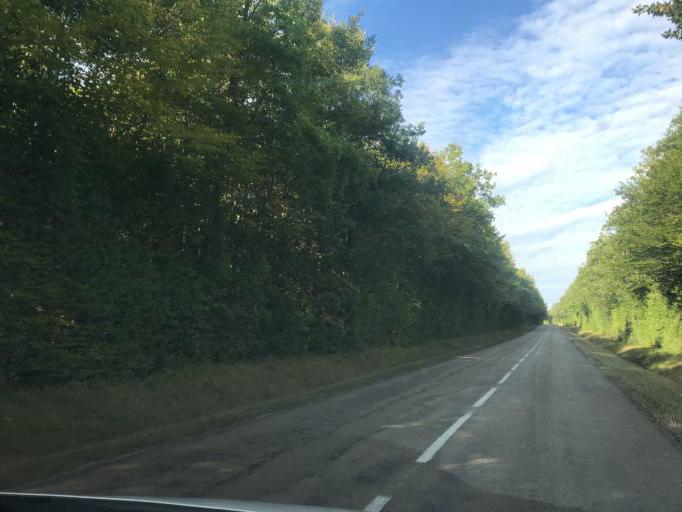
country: FR
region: Bourgogne
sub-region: Departement de l'Yonne
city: Fontenailles
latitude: 47.5672
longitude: 3.4469
